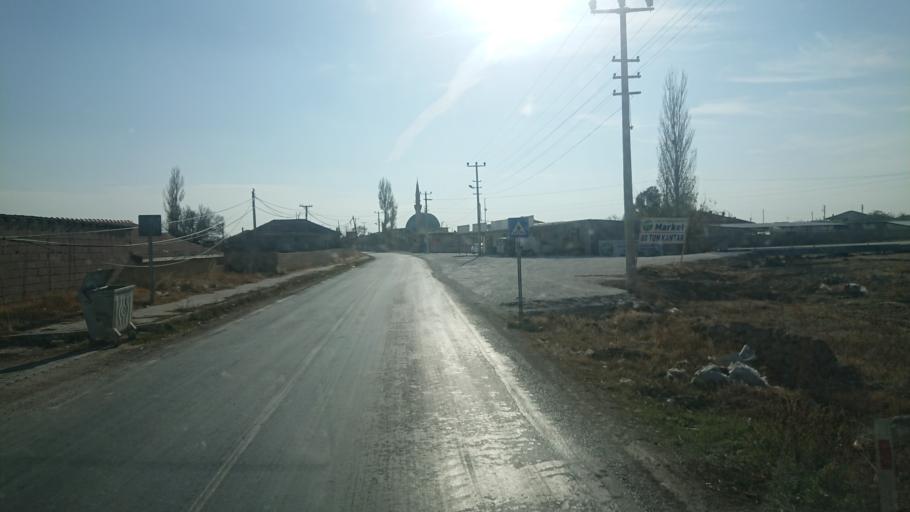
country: TR
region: Aksaray
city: Sultanhani
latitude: 38.1454
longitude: 33.5023
